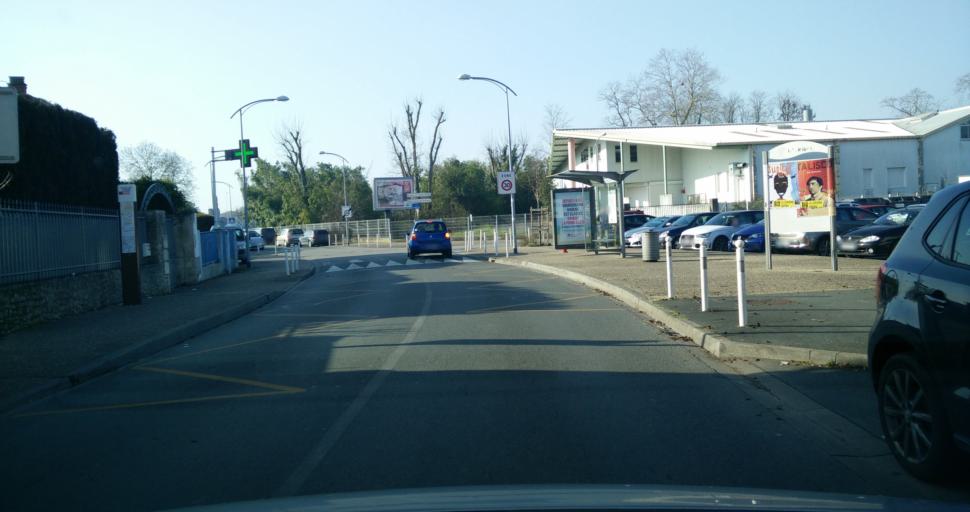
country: FR
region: Poitou-Charentes
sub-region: Departement de la Charente-Maritime
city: La Rochelle
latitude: 46.1743
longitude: -1.1452
